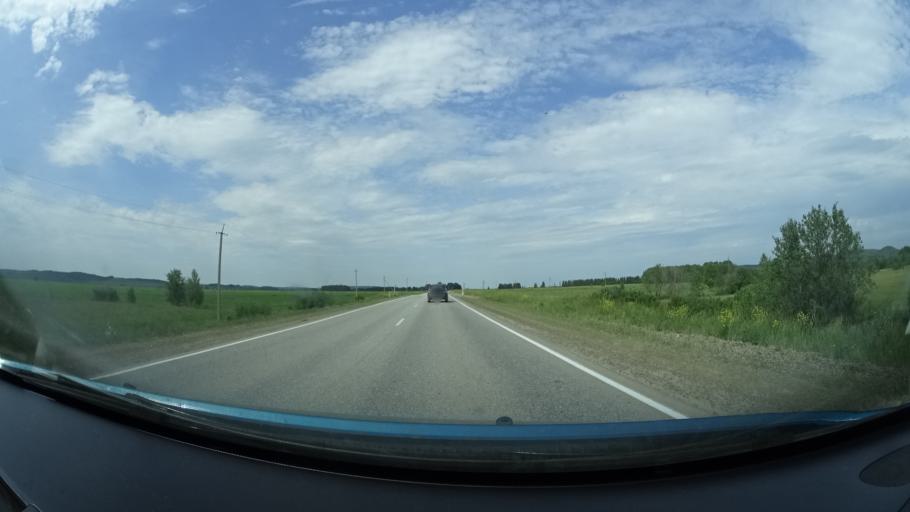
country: RU
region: Perm
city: Barda
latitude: 57.0581
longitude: 55.5423
